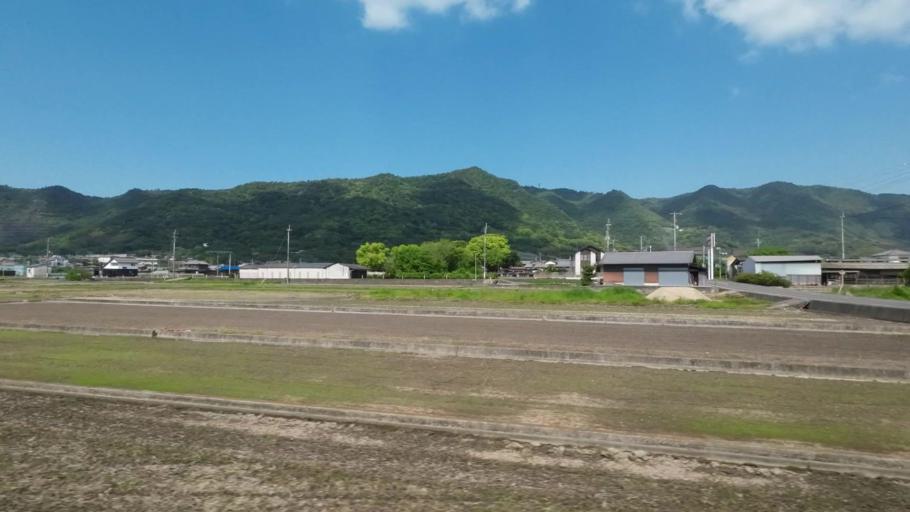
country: JP
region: Kagawa
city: Kan'onjicho
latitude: 34.1567
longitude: 133.6884
